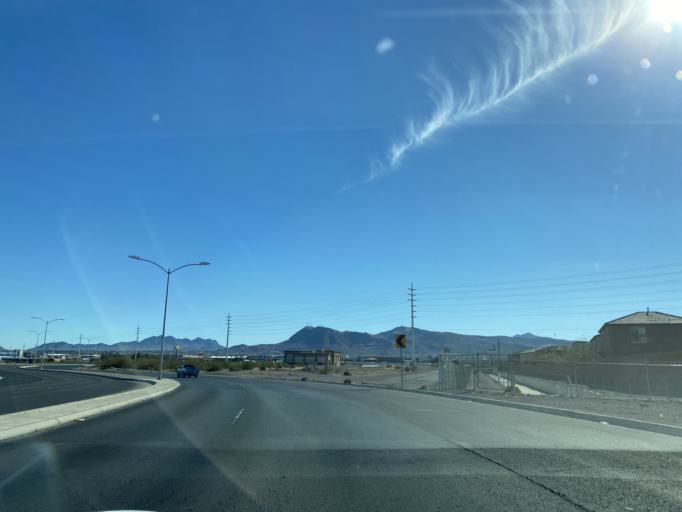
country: US
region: Nevada
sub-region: Clark County
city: Henderson
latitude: 36.0669
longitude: -115.0288
